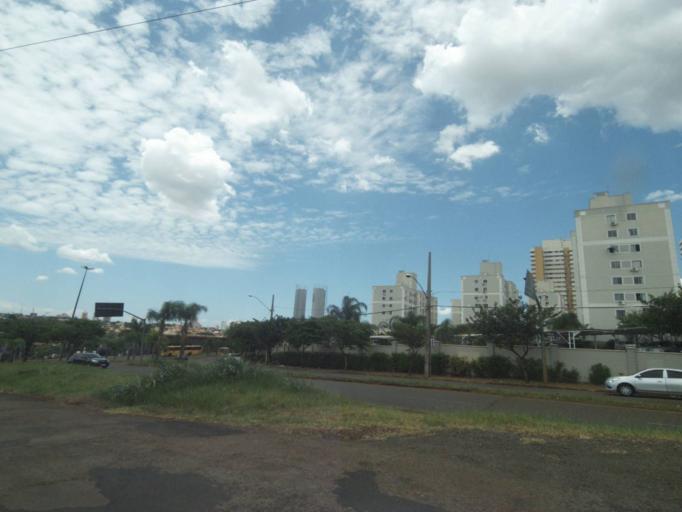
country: BR
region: Parana
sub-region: Londrina
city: Londrina
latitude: -23.3220
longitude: -51.1941
